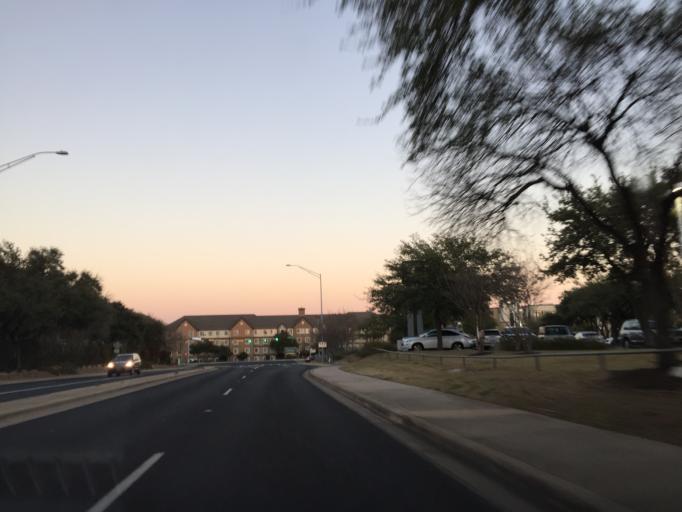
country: US
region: Texas
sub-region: Williamson County
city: Jollyville
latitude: 30.3932
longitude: -97.7413
